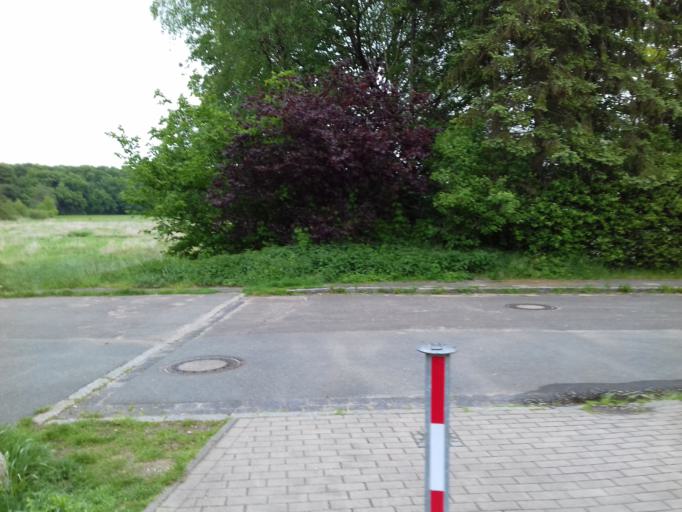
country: DE
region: Schleswig-Holstein
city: Neumunster
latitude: 54.0785
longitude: 10.0070
